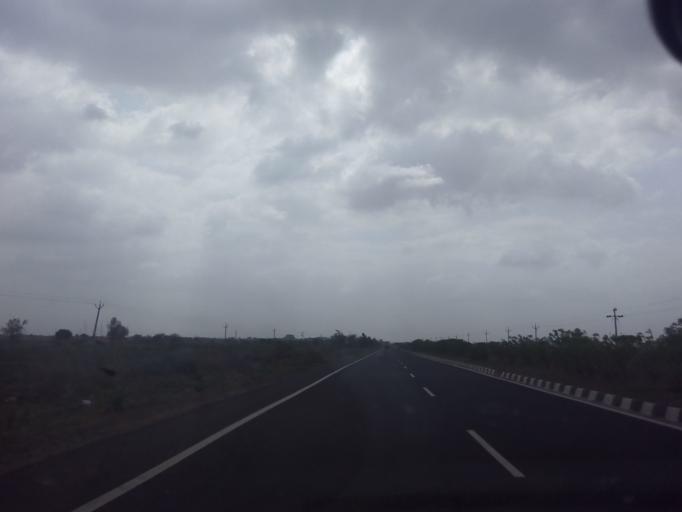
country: IN
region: Gujarat
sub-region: Surendranagar
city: Halvad
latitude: 23.0052
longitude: 71.1311
